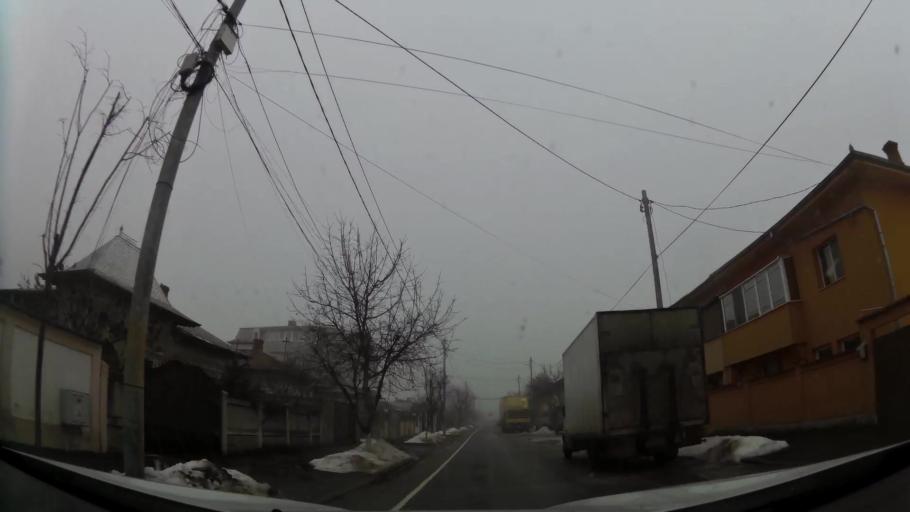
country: RO
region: Ilfov
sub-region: Comuna Chiajna
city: Chiajna
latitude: 44.4595
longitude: 25.9823
